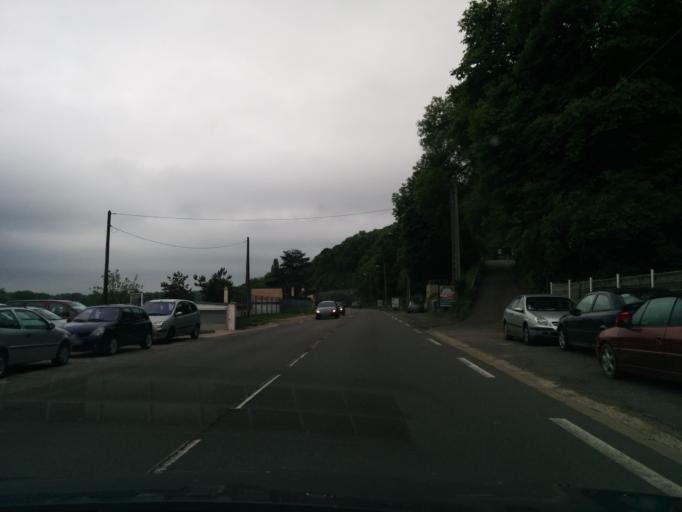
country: FR
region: Ile-de-France
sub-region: Departement des Yvelines
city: Rosny-sur-Seine
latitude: 49.0156
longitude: 1.6110
